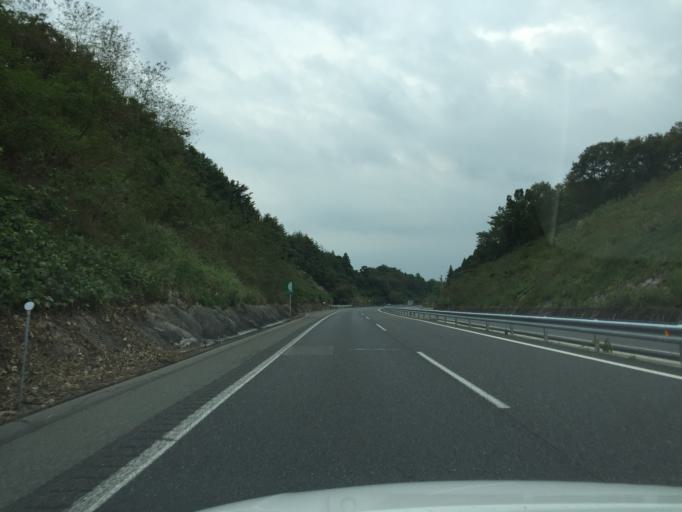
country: JP
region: Fukushima
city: Iwaki
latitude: 37.0805
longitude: 140.7892
